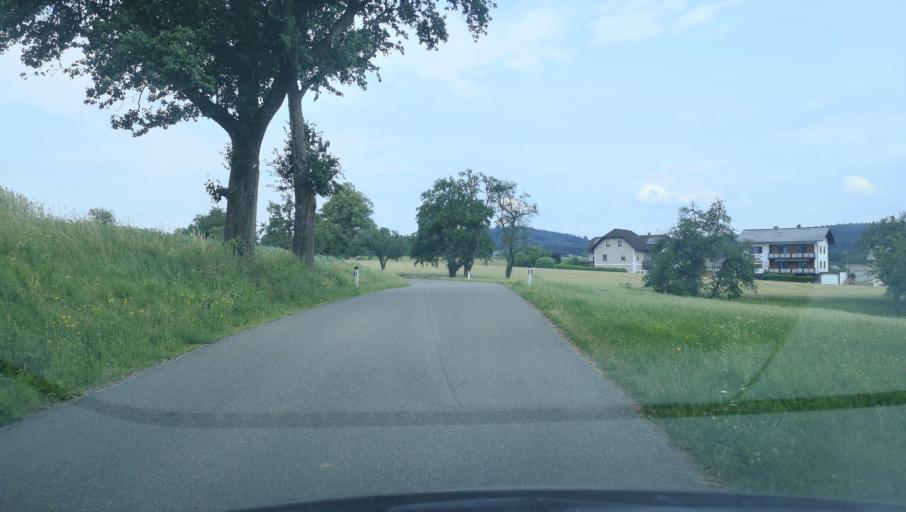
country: AT
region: Lower Austria
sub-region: Politischer Bezirk Melk
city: Blindenmarkt
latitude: 48.1401
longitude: 14.9893
